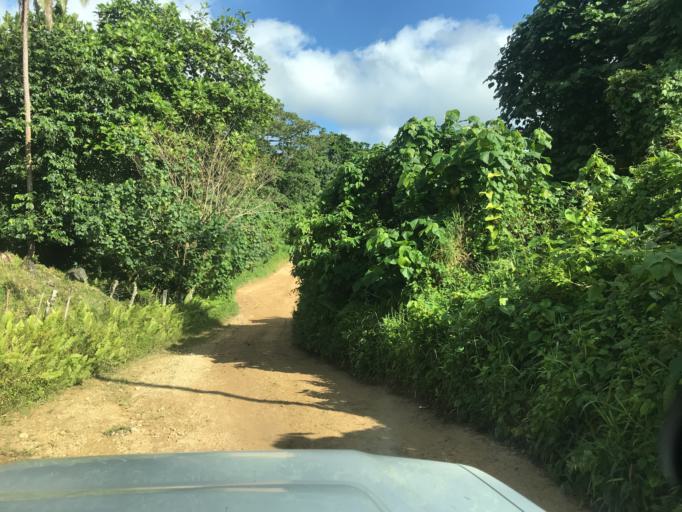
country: VU
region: Sanma
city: Luganville
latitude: -15.5058
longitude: 167.0985
